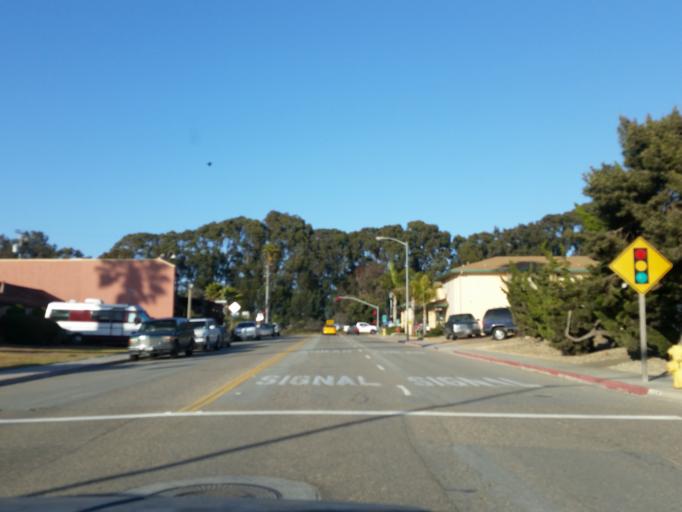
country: US
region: California
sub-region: San Luis Obispo County
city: Oceano
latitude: 35.1069
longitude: -120.6247
